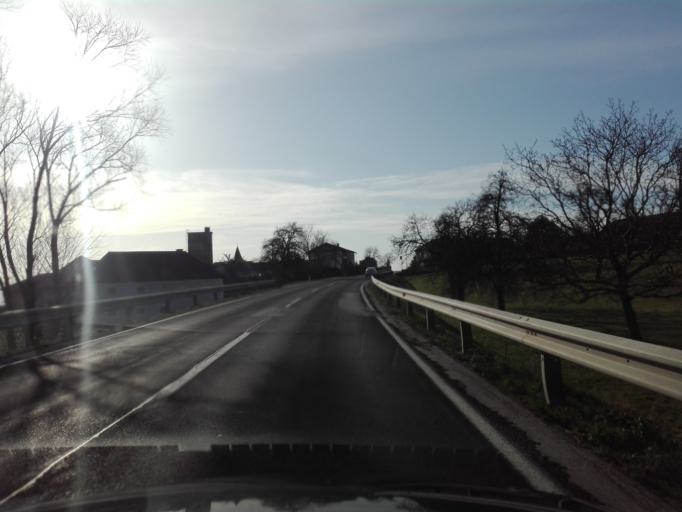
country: AT
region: Lower Austria
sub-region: Politischer Bezirk Amstetten
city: Strengberg
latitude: 48.1606
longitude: 14.6167
